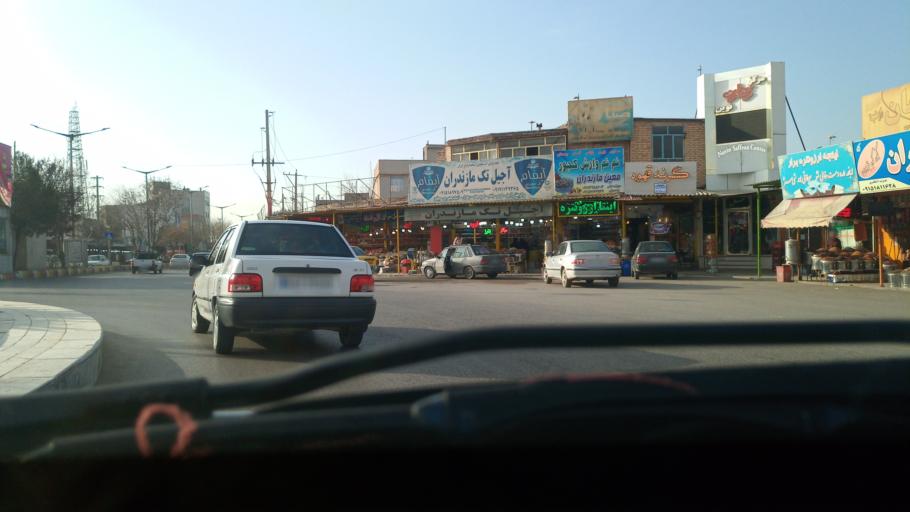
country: IR
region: Khorasan-e Shomali
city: Faruj
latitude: 37.2324
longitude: 58.2194
